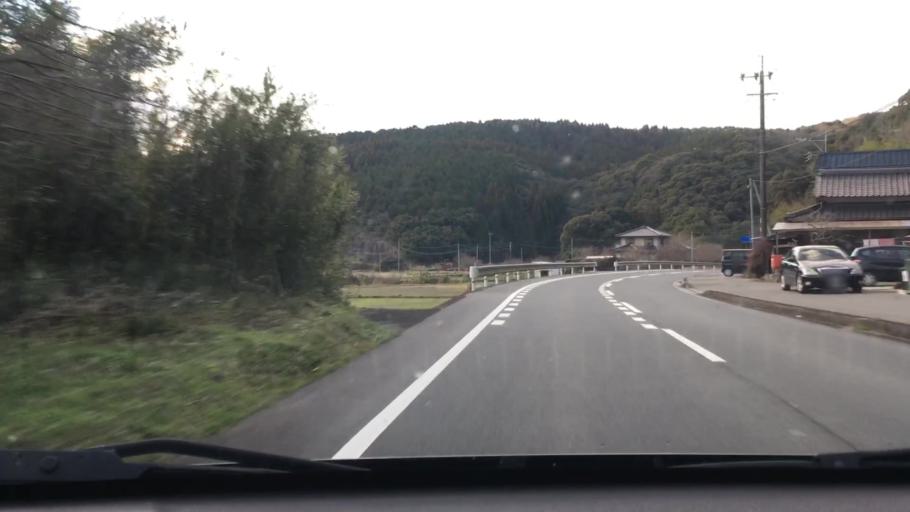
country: JP
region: Oita
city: Hiji
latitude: 33.4217
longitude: 131.4166
